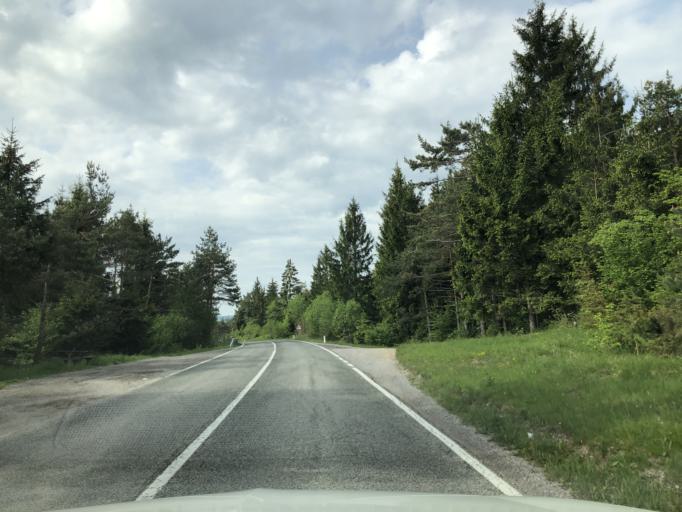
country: SI
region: Bloke
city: Nova Vas
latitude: 45.7665
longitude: 14.4815
